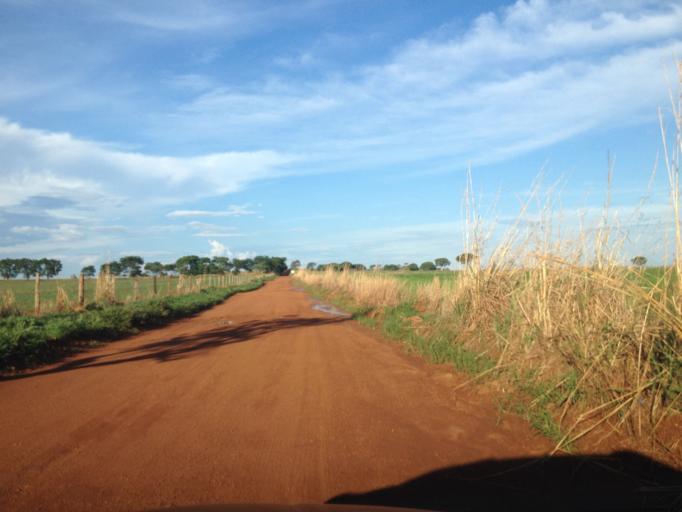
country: BR
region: Goias
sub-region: Abadiania
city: Abadiania
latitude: -15.9938
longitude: -48.5388
